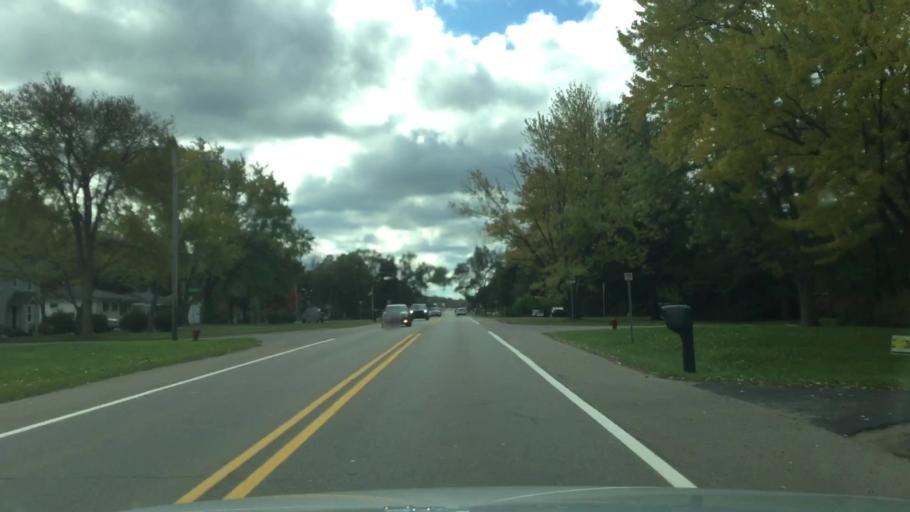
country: US
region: Michigan
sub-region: Oakland County
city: Clarkston
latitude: 42.7288
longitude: -83.4189
